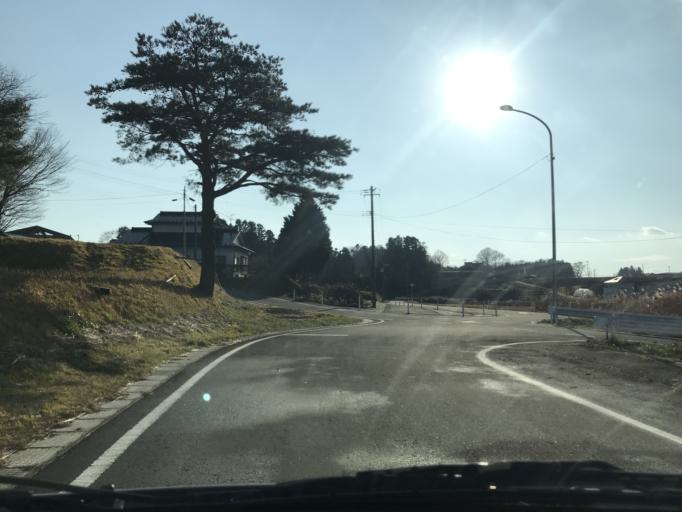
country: JP
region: Miyagi
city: Wakuya
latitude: 38.6800
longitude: 141.1169
